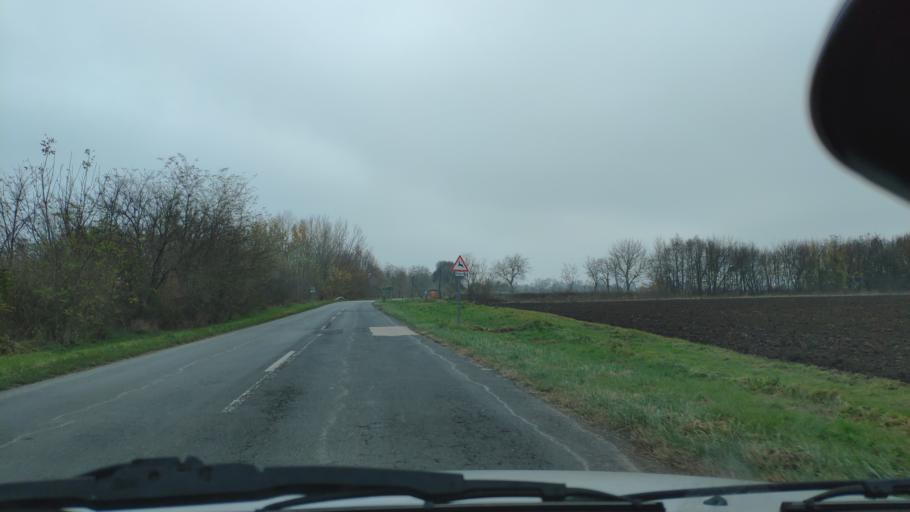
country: HU
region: Somogy
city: Balatonbereny
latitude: 46.6820
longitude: 17.2839
